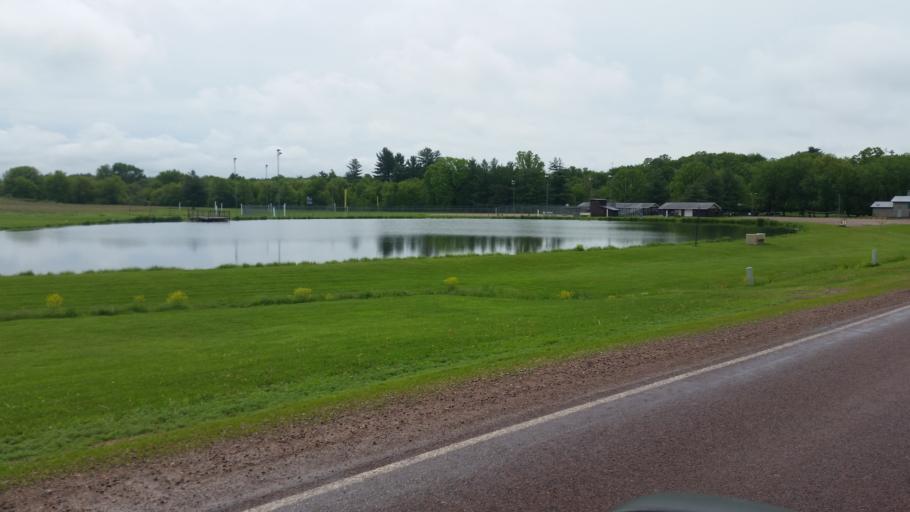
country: US
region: Wisconsin
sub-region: Clark County
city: Neillsville
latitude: 44.5933
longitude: -90.4616
